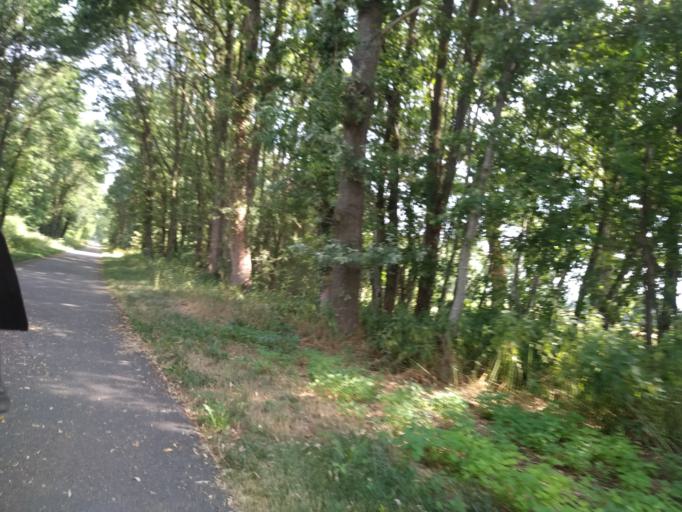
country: FR
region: Bourgogne
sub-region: Departement de Saone-et-Loire
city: Saint-Yan
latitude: 46.3452
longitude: 4.0283
